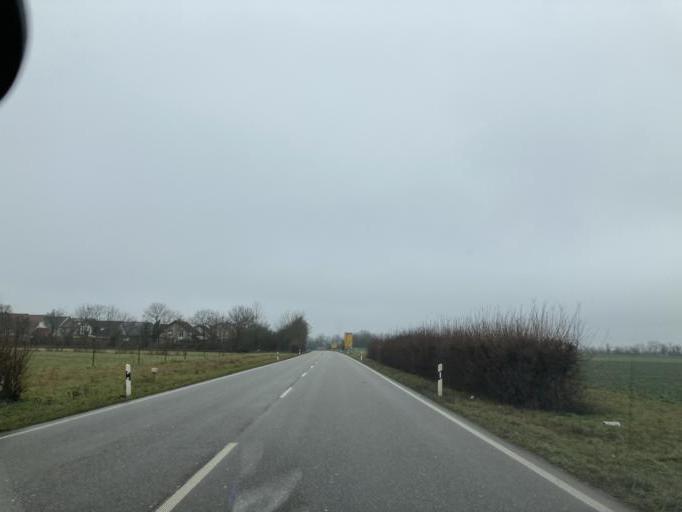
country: DE
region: Baden-Wuerttemberg
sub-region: Freiburg Region
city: Neuenburg am Rhein
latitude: 47.8188
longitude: 7.5759
